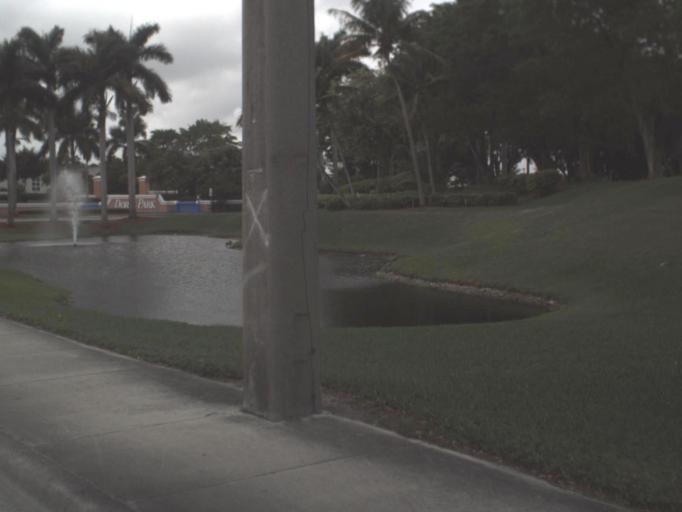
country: US
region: Florida
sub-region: Miami-Dade County
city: Doral
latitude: 25.8118
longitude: -80.3606
